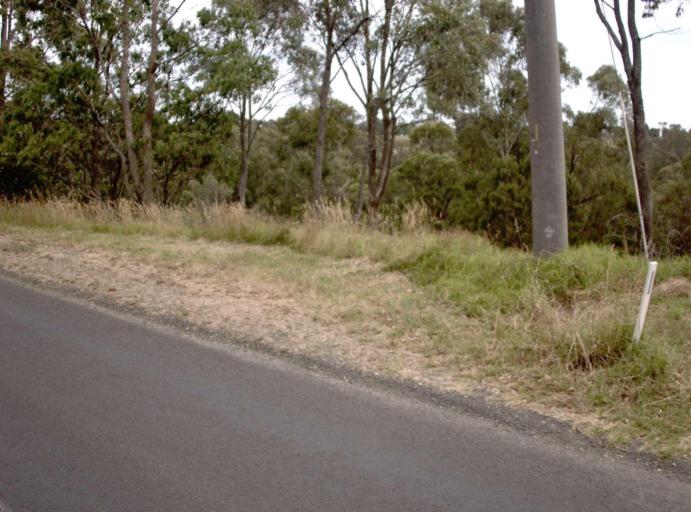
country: AU
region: Victoria
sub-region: Latrobe
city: Traralgon
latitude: -38.1347
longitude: 146.4762
